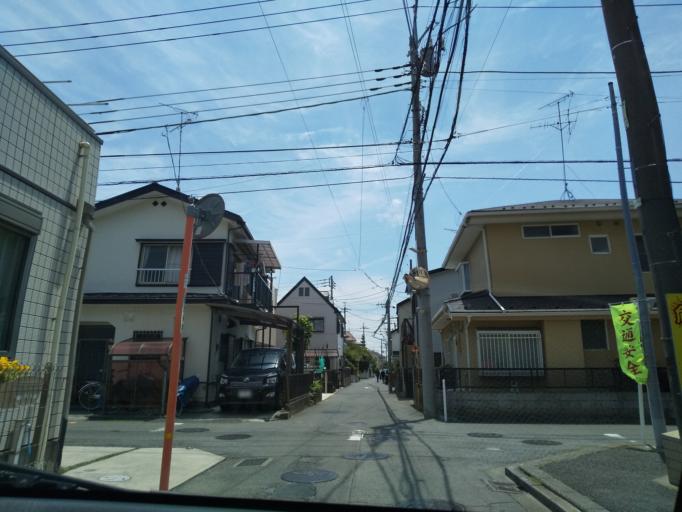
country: JP
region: Tokyo
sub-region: Machida-shi
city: Machida
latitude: 35.5525
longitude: 139.4007
